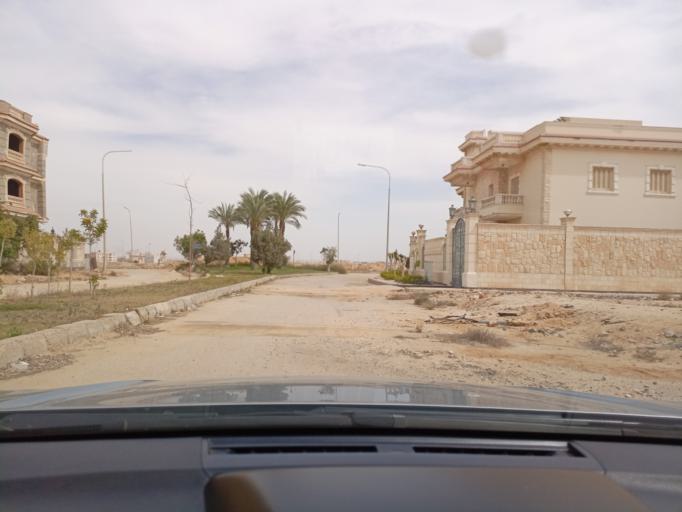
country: EG
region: Muhafazat al Qalyubiyah
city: Al Khankah
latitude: 30.2492
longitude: 31.5049
